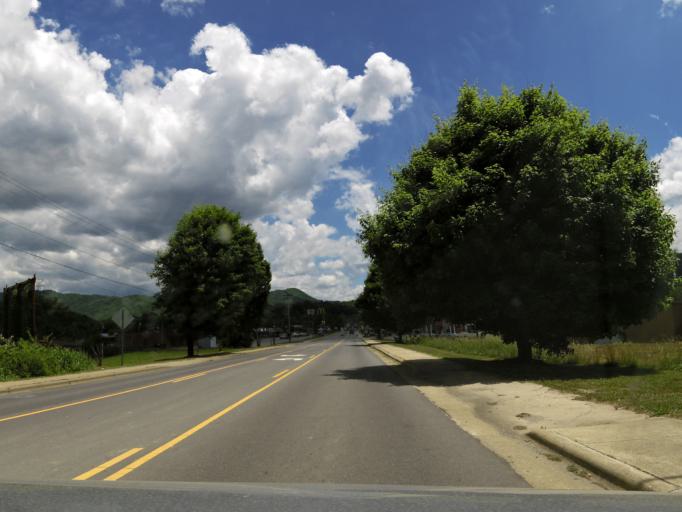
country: US
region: North Carolina
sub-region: Graham County
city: Robbinsville
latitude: 35.3279
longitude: -83.8061
